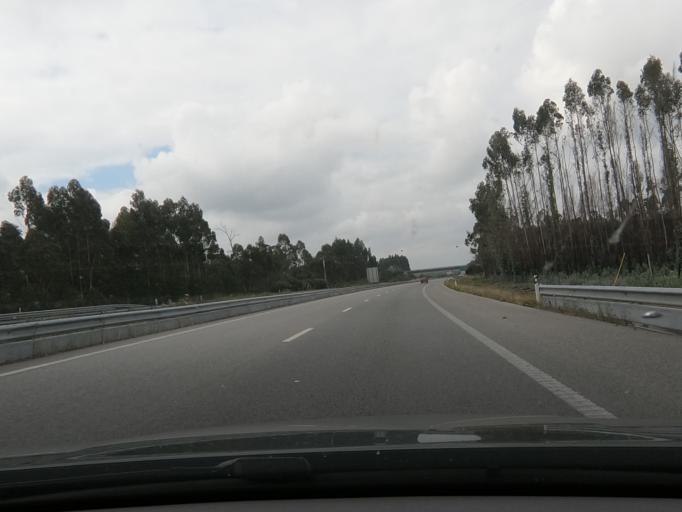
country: PT
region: Coimbra
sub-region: Mira
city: Mira
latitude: 40.4015
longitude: -8.7094
